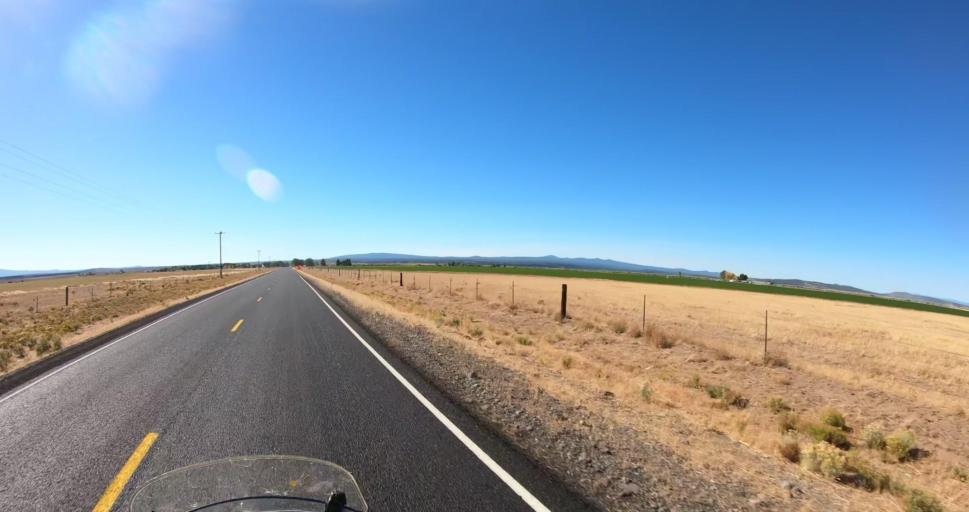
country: US
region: Oregon
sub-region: Deschutes County
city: La Pine
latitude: 43.1277
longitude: -121.0267
